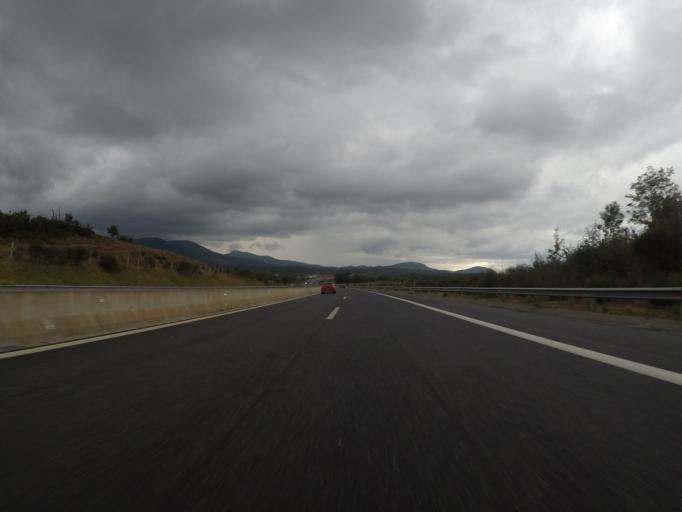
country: GR
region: Peloponnese
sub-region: Nomos Arkadias
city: Megalopoli
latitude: 37.3561
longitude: 22.1216
